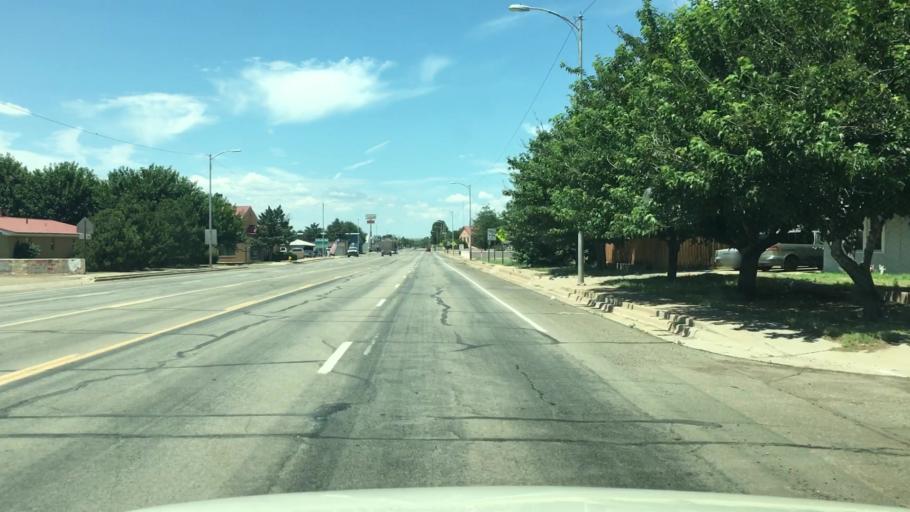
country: US
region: New Mexico
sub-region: De Baca County
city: Fort Sumner
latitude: 34.4698
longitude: -104.2392
